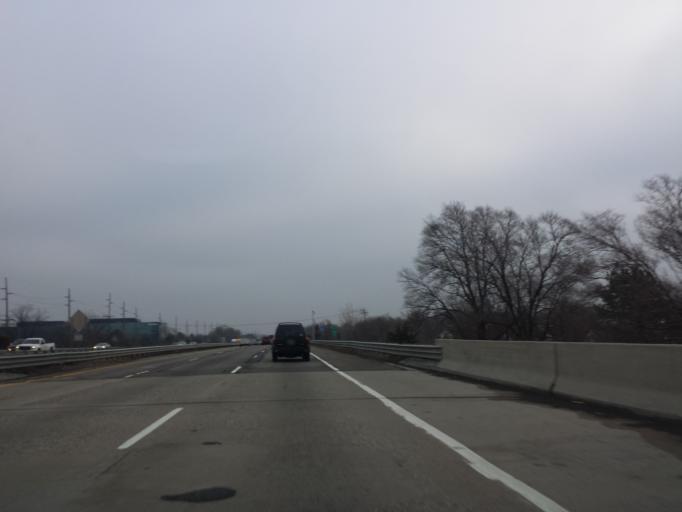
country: US
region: Michigan
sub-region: Oakland County
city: Clawson
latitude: 42.5589
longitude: -83.1475
